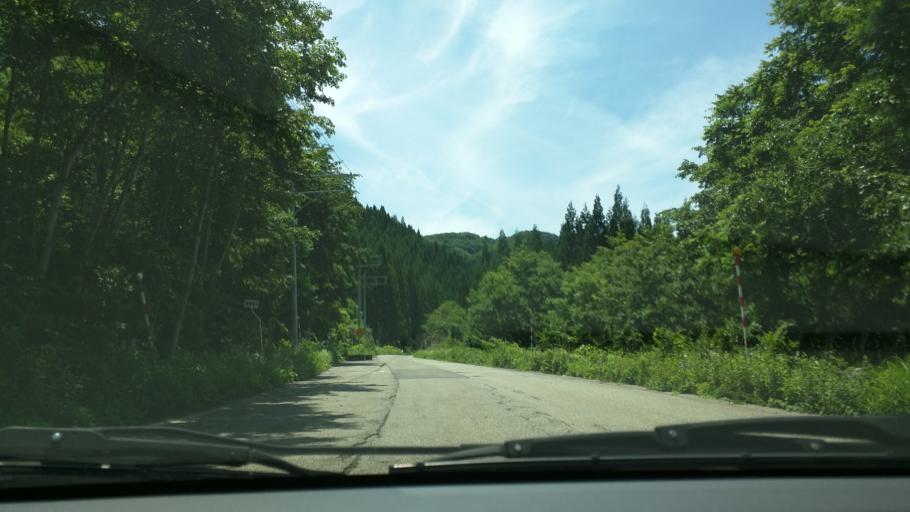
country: JP
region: Fukushima
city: Kitakata
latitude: 37.2564
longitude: 139.7486
